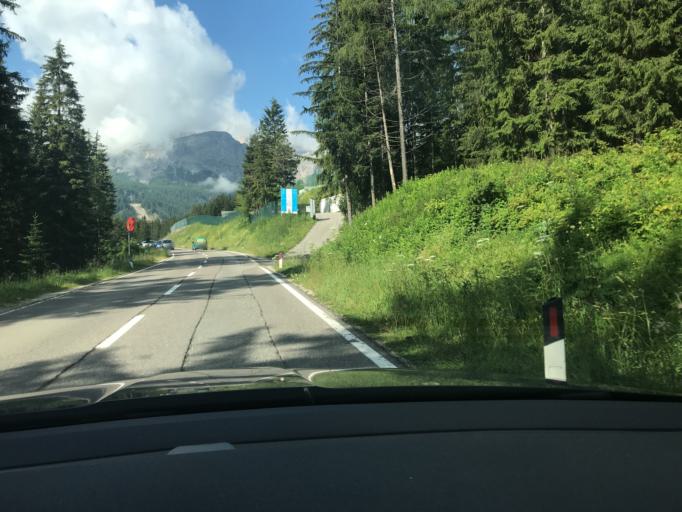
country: IT
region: Trentino-Alto Adige
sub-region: Bolzano
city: Corvara in Badia
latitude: 46.5642
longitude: 11.8861
